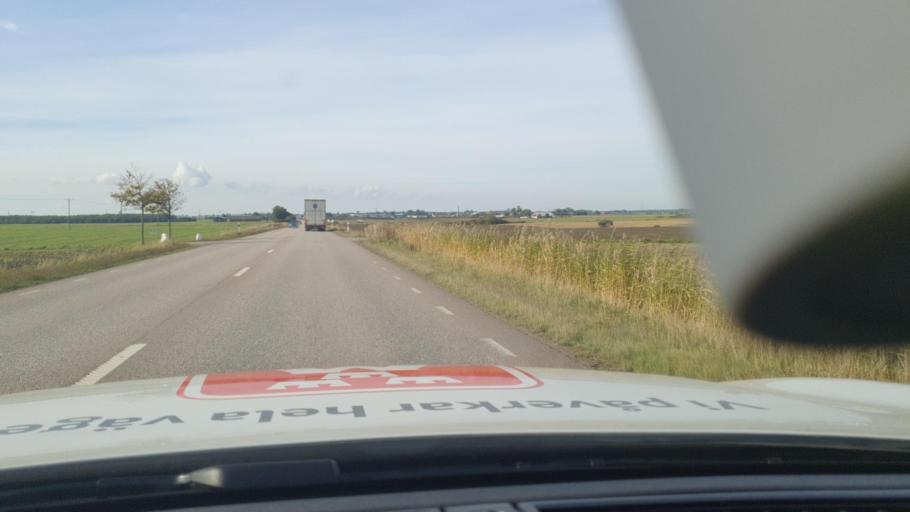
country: SE
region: Skane
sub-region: Angelholms Kommun
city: Munka-Ljungby
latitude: 56.2538
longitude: 12.9386
